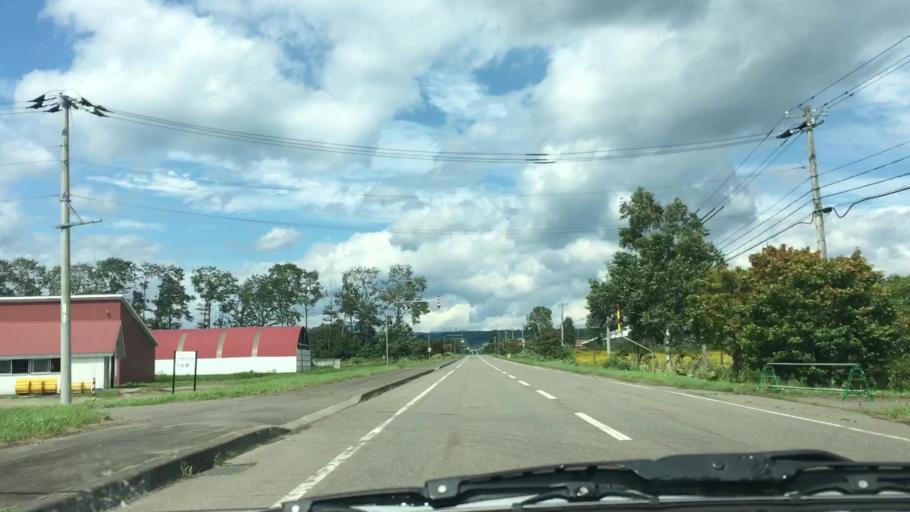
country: JP
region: Hokkaido
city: Otofuke
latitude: 43.2858
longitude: 143.3071
